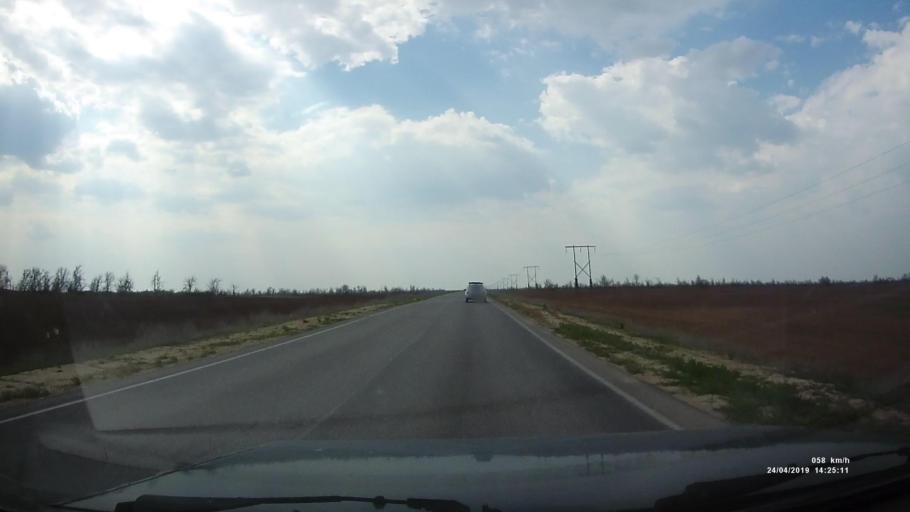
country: RU
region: Kalmykiya
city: Arshan'
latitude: 46.3301
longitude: 44.0844
